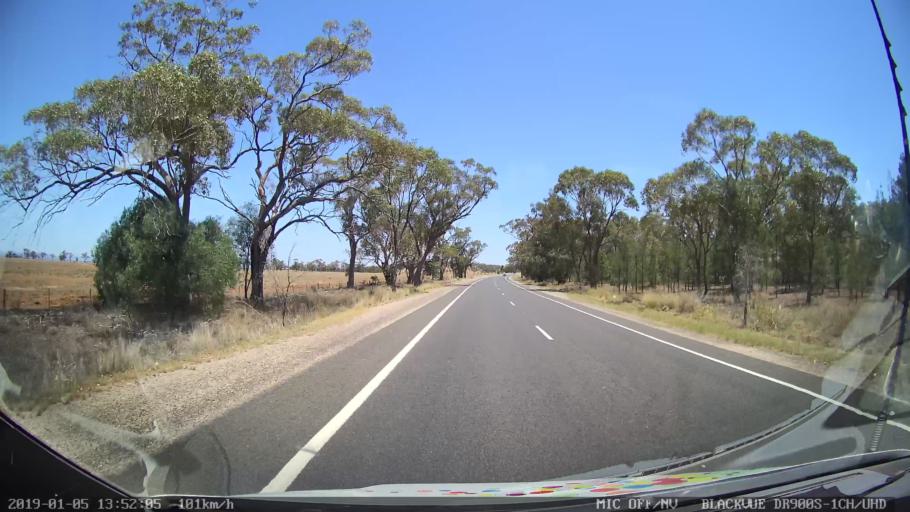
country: AU
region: New South Wales
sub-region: Gunnedah
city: Gunnedah
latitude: -31.0545
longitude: 150.2780
